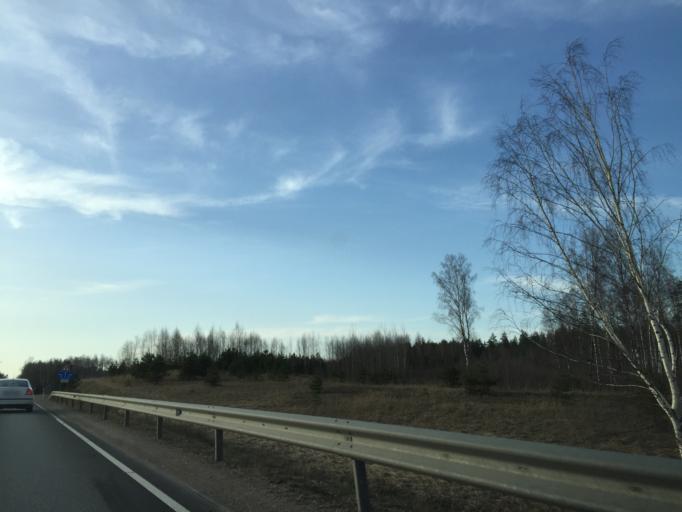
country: LV
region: Ikskile
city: Ikskile
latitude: 56.8843
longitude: 24.4990
